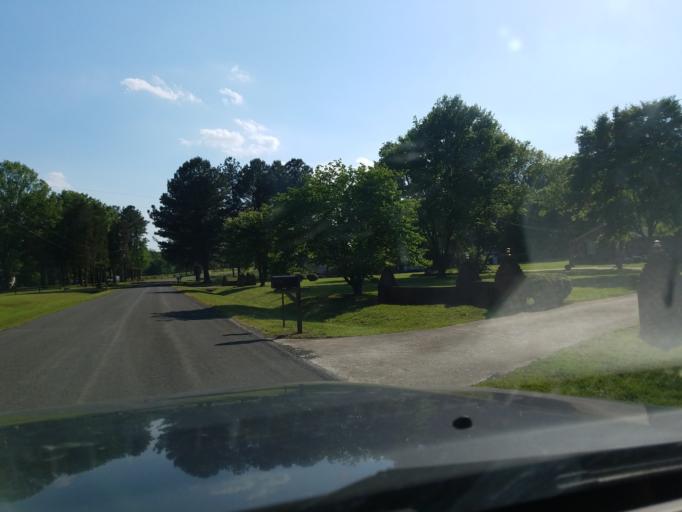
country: US
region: North Carolina
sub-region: Vance County
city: Henderson
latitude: 36.4048
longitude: -78.3857
